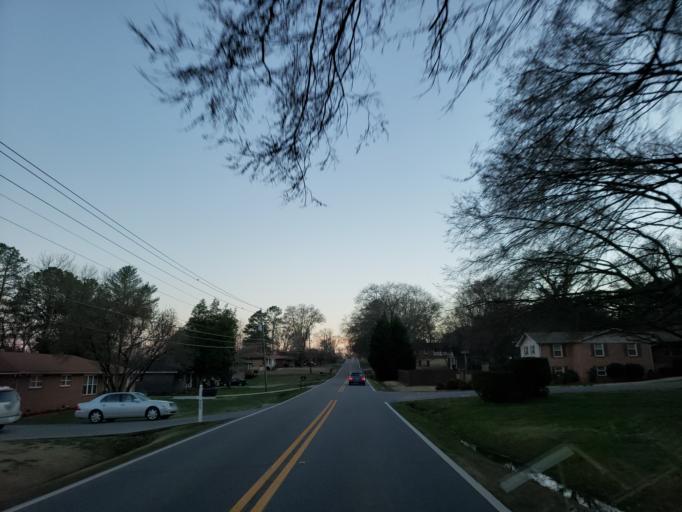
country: US
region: Georgia
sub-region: Bartow County
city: Cartersville
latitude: 34.1988
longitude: -84.8196
